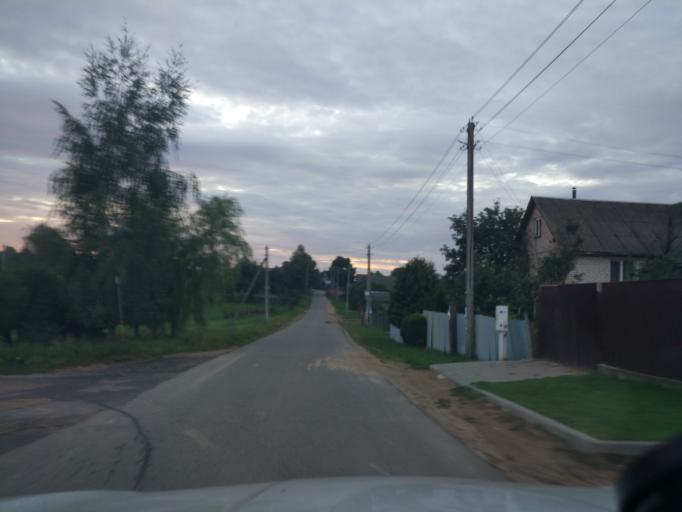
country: BY
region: Minsk
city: Astrashytski Haradok
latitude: 54.0827
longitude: 27.7060
